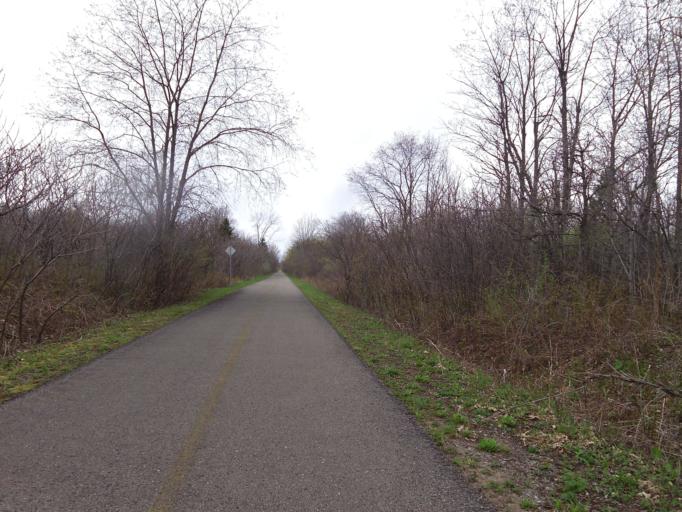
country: CA
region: Quebec
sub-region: Laurentides
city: Brownsburg-Chatham
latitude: 45.5805
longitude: -74.4088
